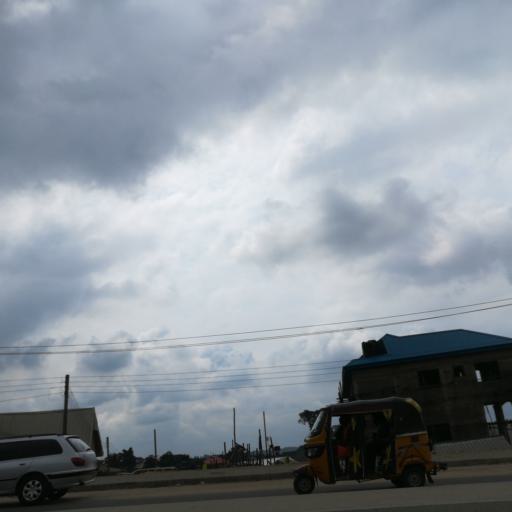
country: NG
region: Rivers
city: Port Harcourt
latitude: 4.8289
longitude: 7.0700
